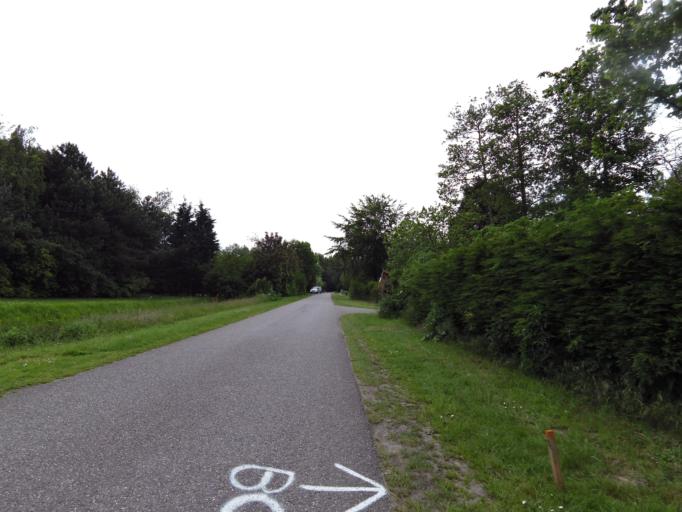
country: NL
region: South Holland
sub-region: Gemeente Hellevoetsluis
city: Nieuw-Helvoet
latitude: 51.8617
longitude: 4.0839
